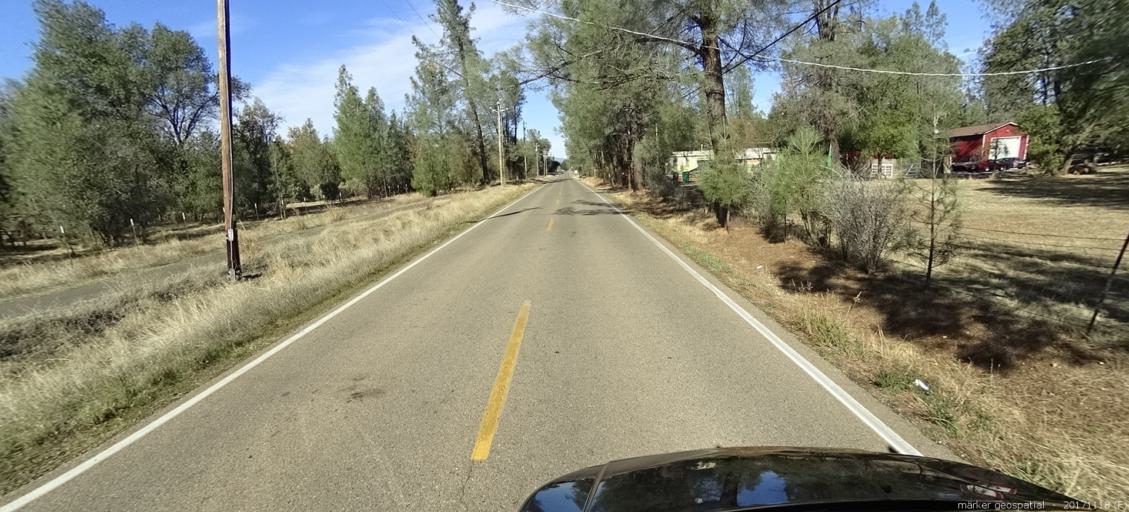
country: US
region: California
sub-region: Shasta County
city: Redding
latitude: 40.4686
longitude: -122.4546
